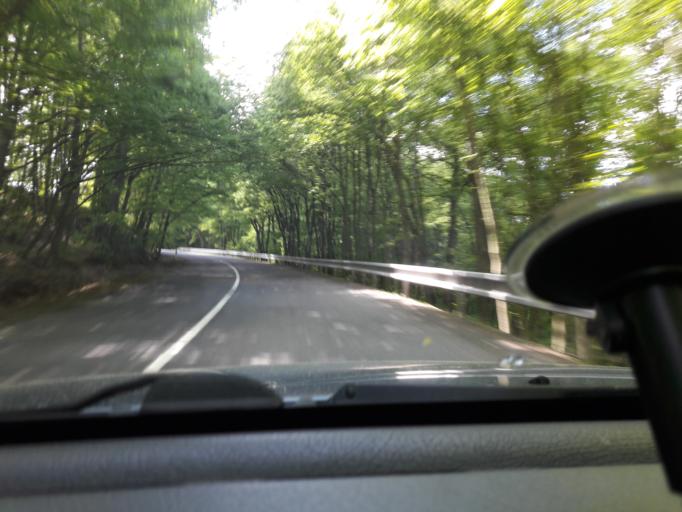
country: SK
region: Banskobystricky
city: Dudince
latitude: 48.2701
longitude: 18.8940
